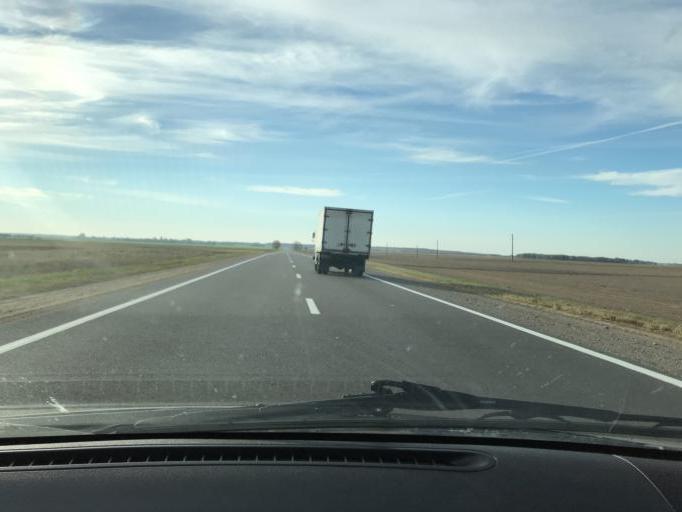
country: BY
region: Brest
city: Ivanava
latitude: 52.1559
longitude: 25.6780
